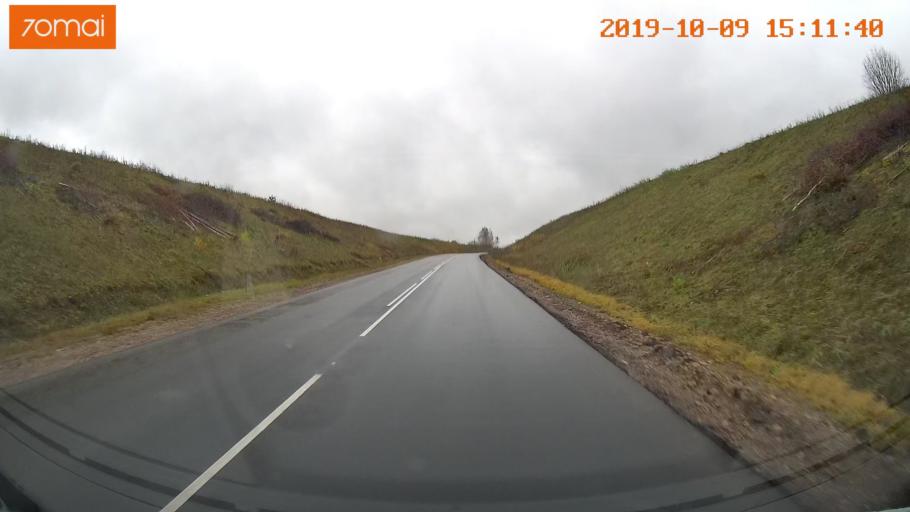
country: RU
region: Kostroma
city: Susanino
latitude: 58.1620
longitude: 41.6288
